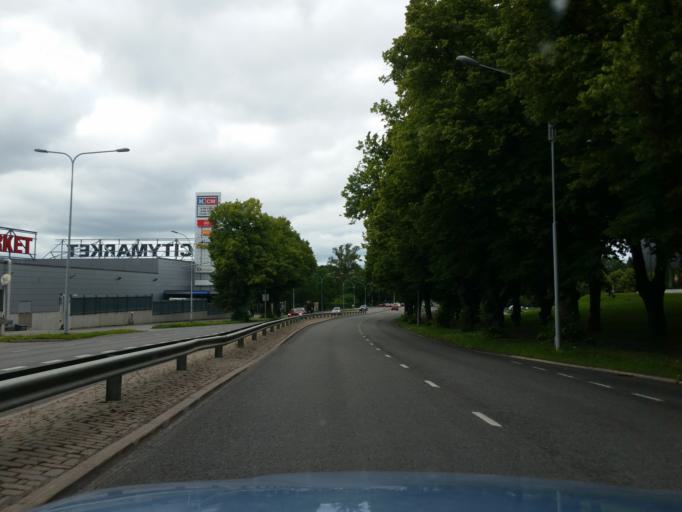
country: FI
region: Varsinais-Suomi
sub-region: Turku
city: Turku
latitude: 60.4416
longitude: 22.2890
